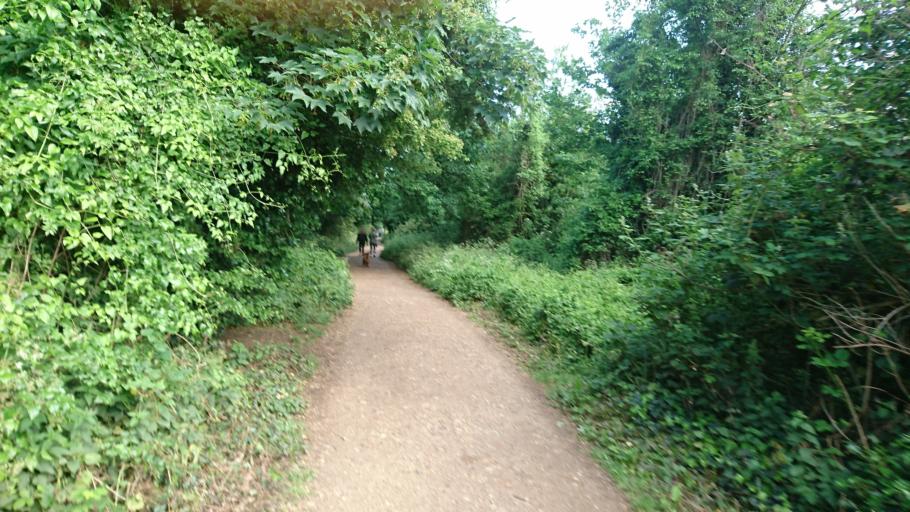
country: GB
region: England
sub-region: Greater London
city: Crouch End
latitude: 51.5730
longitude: -0.1113
